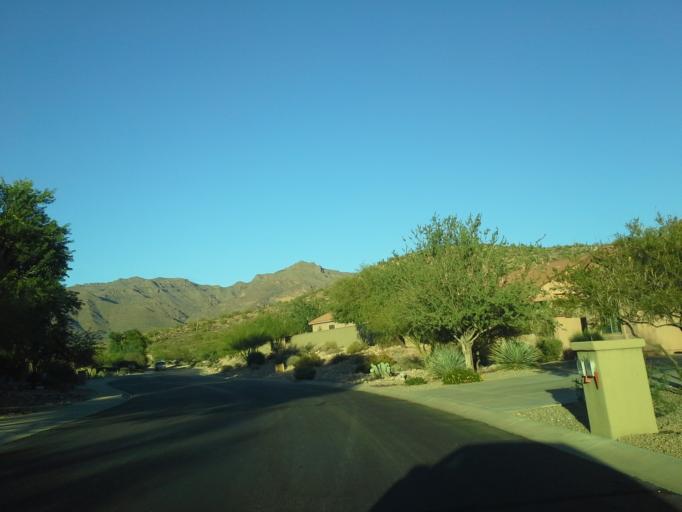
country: US
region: Arizona
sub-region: Pinal County
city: Apache Junction
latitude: 33.3768
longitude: -111.4574
